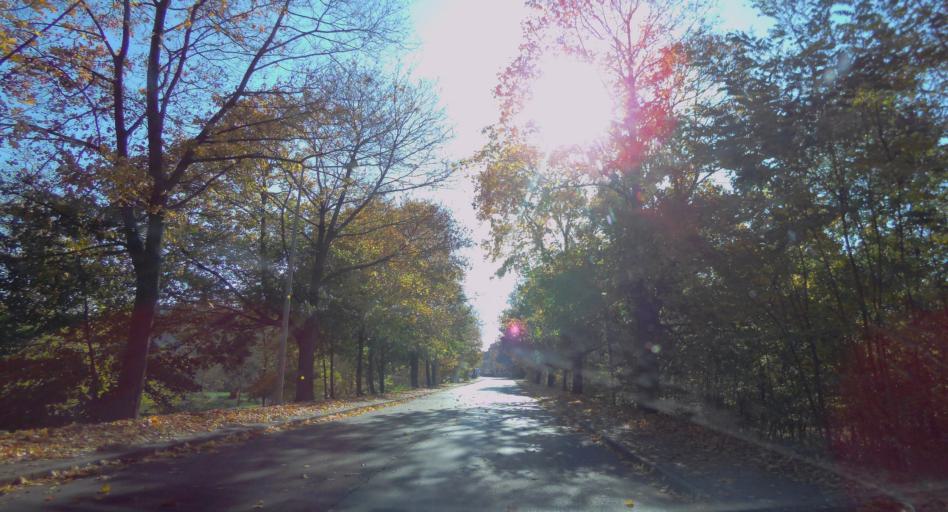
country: PL
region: Subcarpathian Voivodeship
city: Nowa Sarzyna
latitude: 50.3228
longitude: 22.3408
